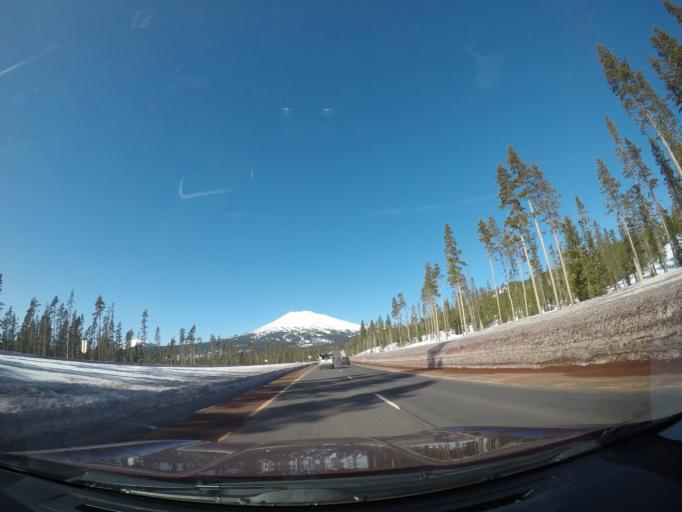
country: US
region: Oregon
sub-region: Deschutes County
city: Sunriver
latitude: 43.9828
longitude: -121.6202
